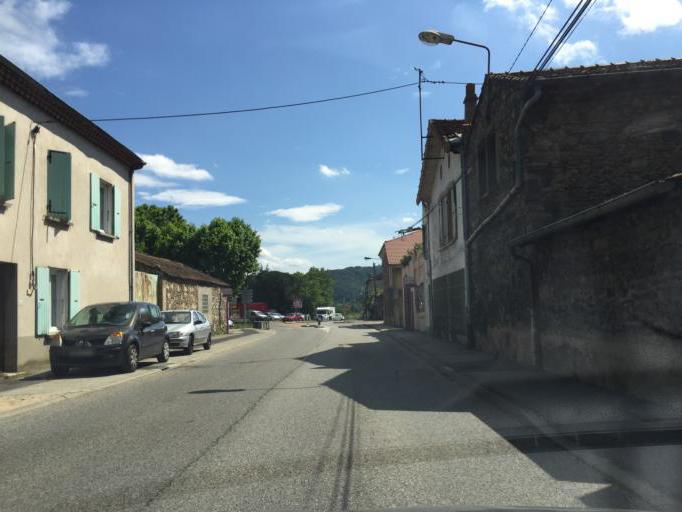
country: FR
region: Rhone-Alpes
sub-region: Departement de la Drome
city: Saint-Vallier
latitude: 45.1402
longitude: 4.8074
